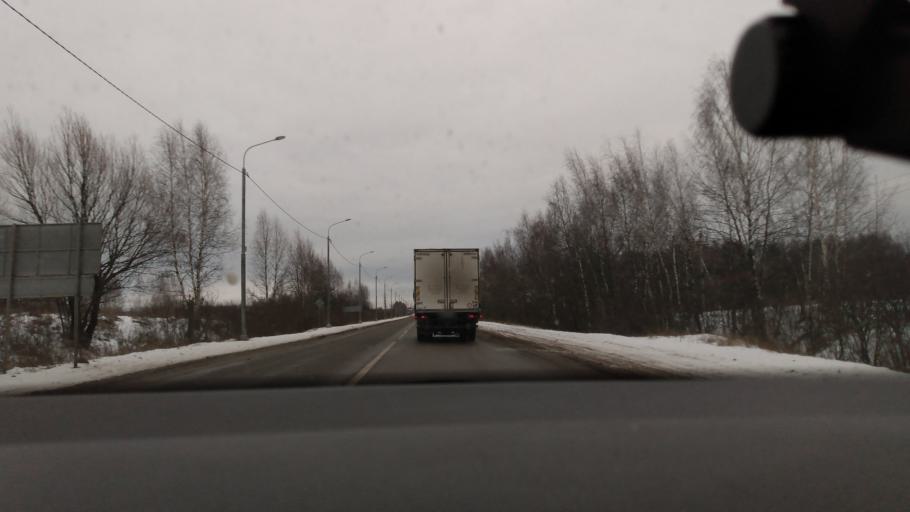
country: RU
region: Moskovskaya
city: Yegor'yevsk
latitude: 55.4130
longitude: 39.0480
